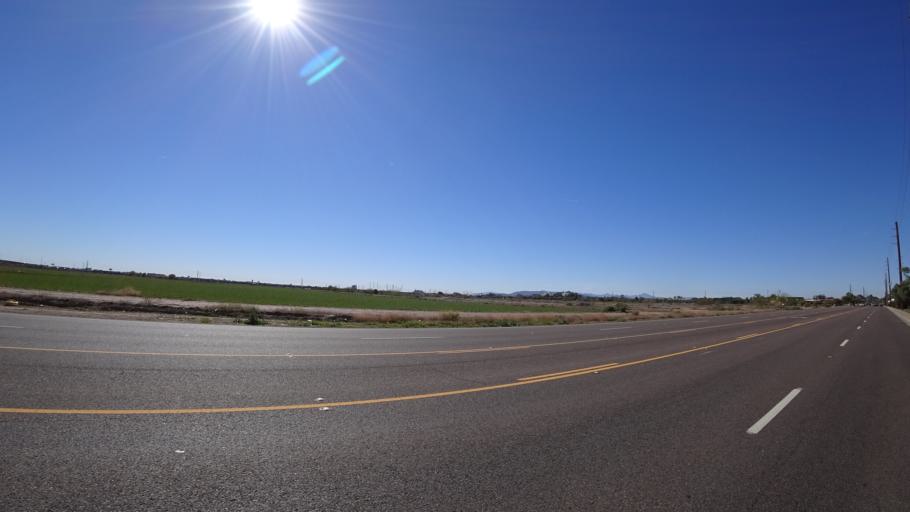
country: US
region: Arizona
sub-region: Maricopa County
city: Tempe
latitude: 33.4514
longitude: -111.9035
